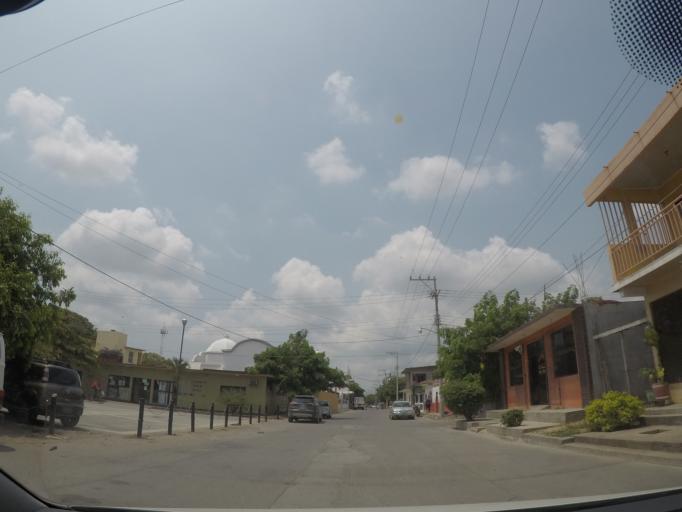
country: MX
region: Oaxaca
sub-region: El Espinal
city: El Espinal
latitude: 16.4852
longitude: -95.0440
